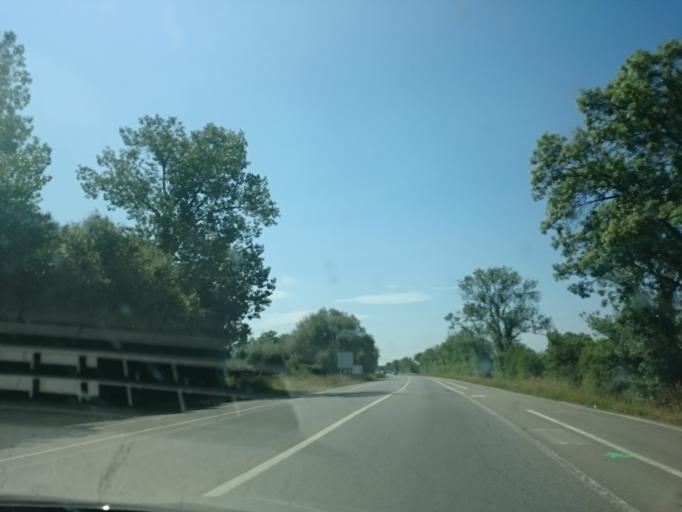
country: FR
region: Pays de la Loire
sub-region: Departement de la Loire-Atlantique
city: Indre
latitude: 47.2049
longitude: -1.6764
